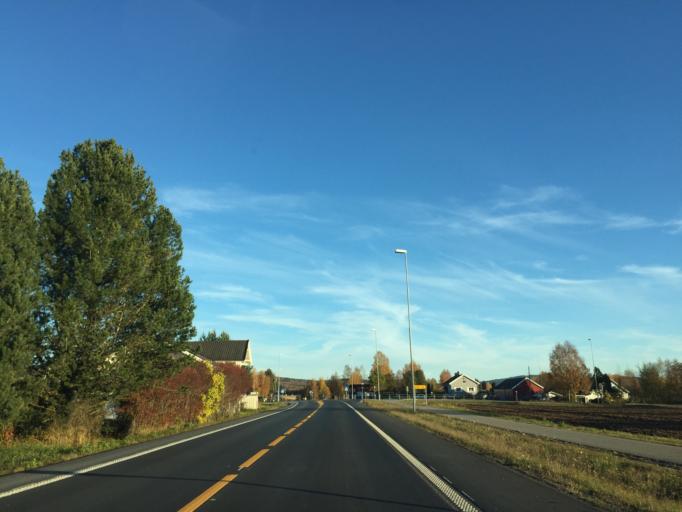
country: NO
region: Hedmark
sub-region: Kongsvinger
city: Spetalen
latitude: 60.2325
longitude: 11.8124
